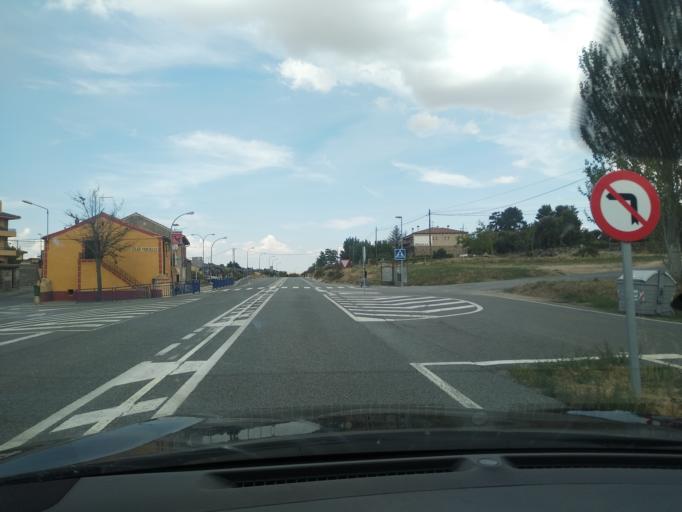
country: ES
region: Castille and Leon
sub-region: Provincia de Segovia
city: Palazuelos de Eresma
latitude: 40.8717
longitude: -4.1007
